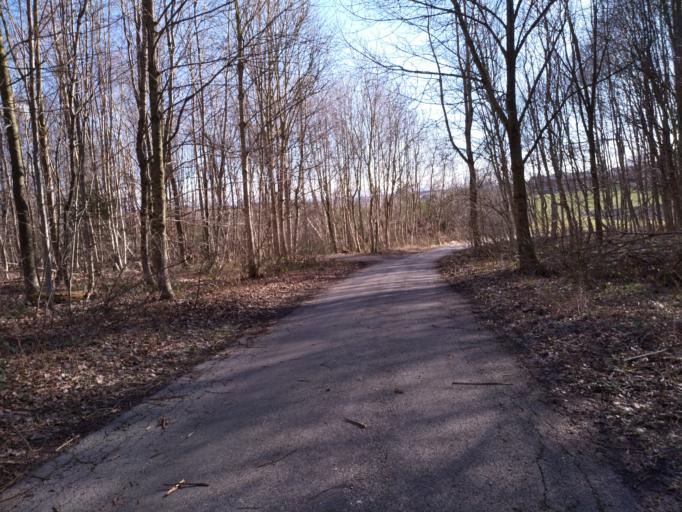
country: DE
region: Bavaria
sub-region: Swabia
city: Baisweil
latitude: 47.9858
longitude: 10.5625
